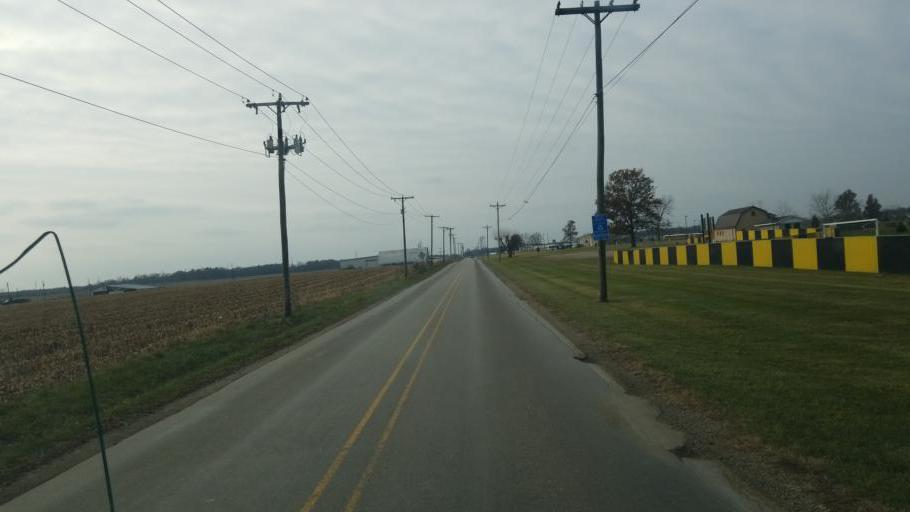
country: US
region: Indiana
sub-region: Adams County
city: Berne
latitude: 40.6431
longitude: -84.9567
